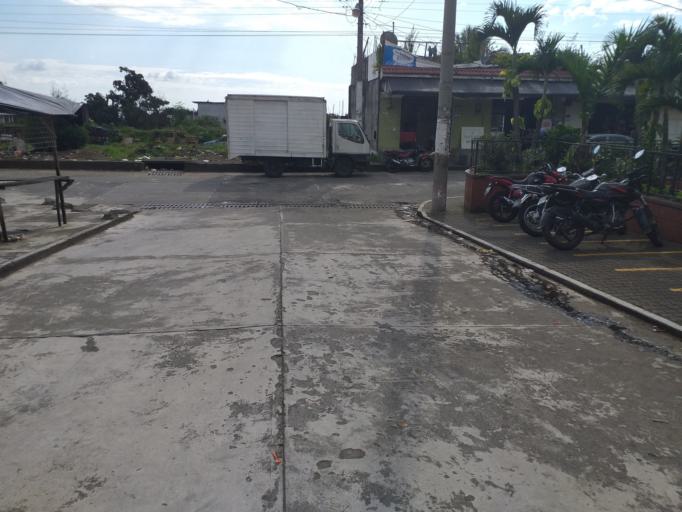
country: GT
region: Suchitepeque
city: Pueblo Nuevo
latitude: 14.6464
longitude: -91.5568
